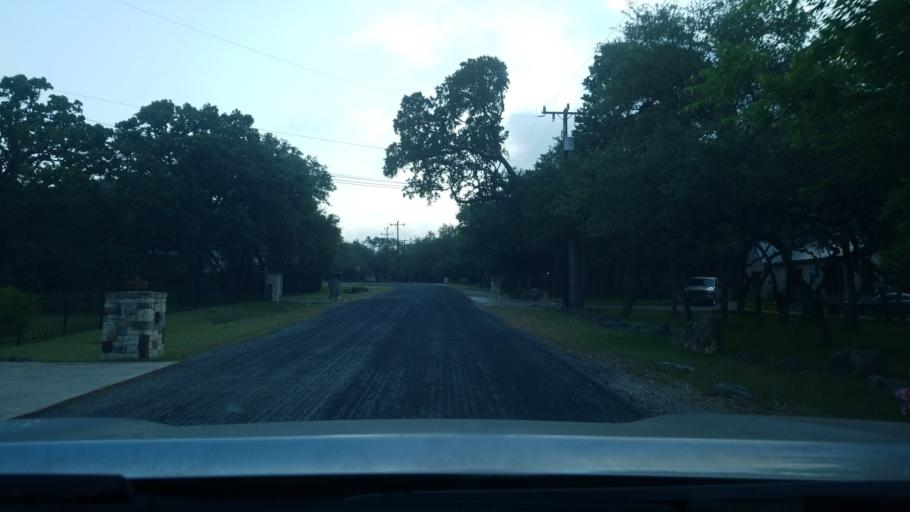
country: US
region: Texas
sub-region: Bexar County
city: Timberwood Park
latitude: 29.6979
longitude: -98.5034
